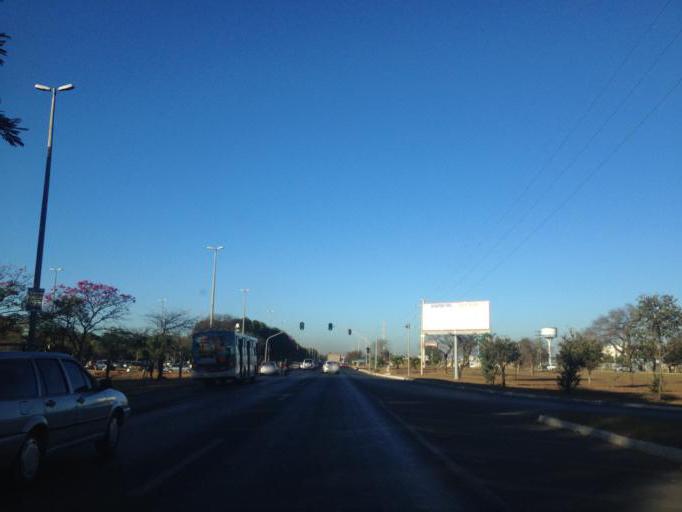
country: BR
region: Federal District
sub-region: Brasilia
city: Brasilia
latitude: -15.7866
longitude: -47.9419
